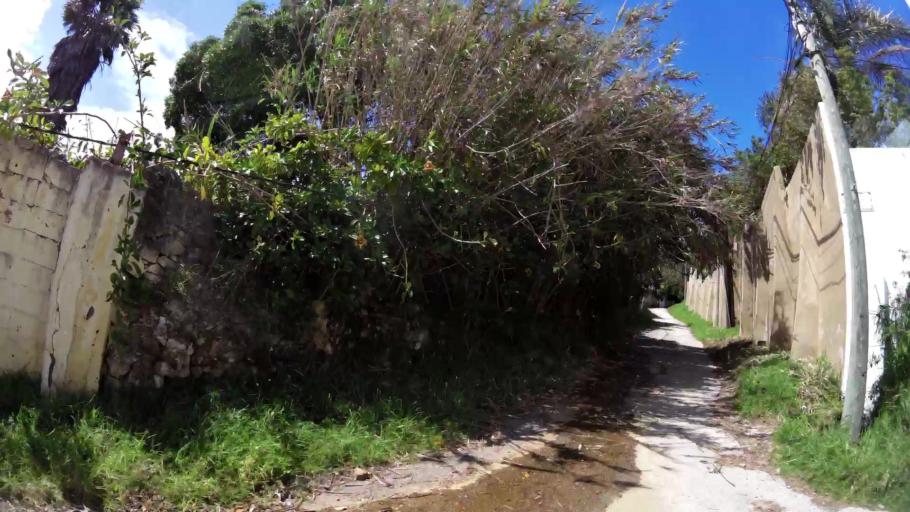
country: MA
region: Tanger-Tetouan
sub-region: Tanger-Assilah
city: Tangier
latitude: 35.7892
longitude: -5.8437
